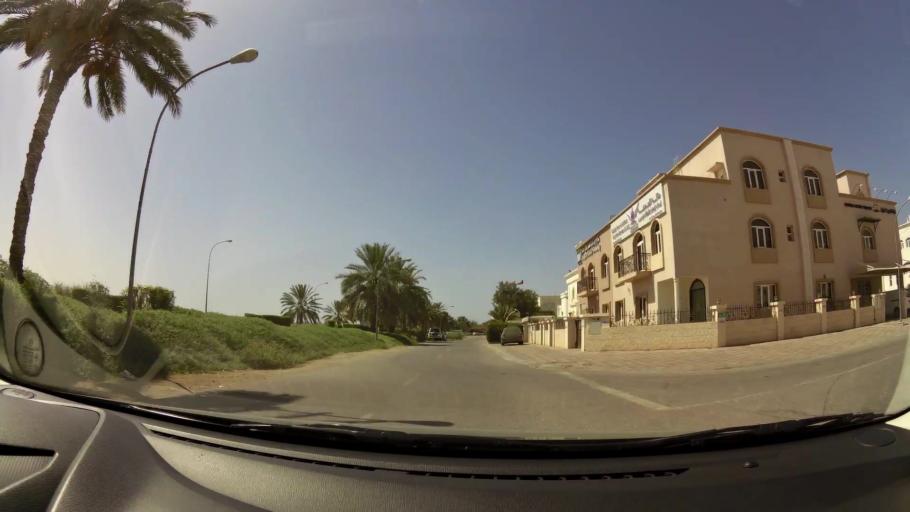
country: OM
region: Muhafazat Masqat
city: Bawshar
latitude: 23.5967
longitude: 58.3477
